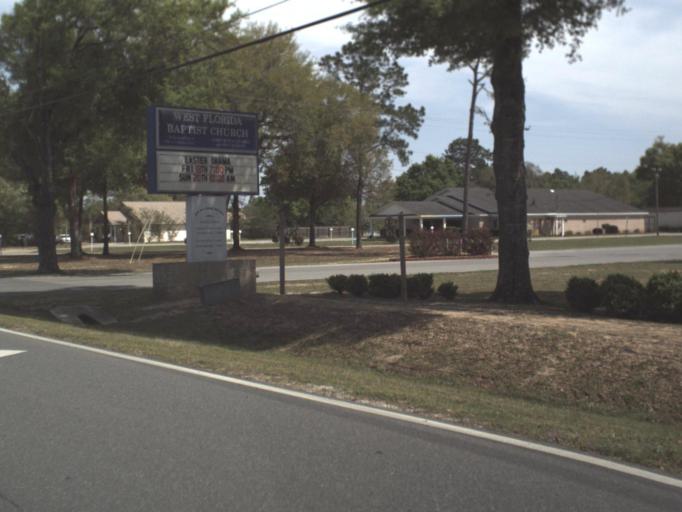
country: US
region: Florida
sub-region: Santa Rosa County
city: Milton
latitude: 30.6026
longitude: -87.0891
